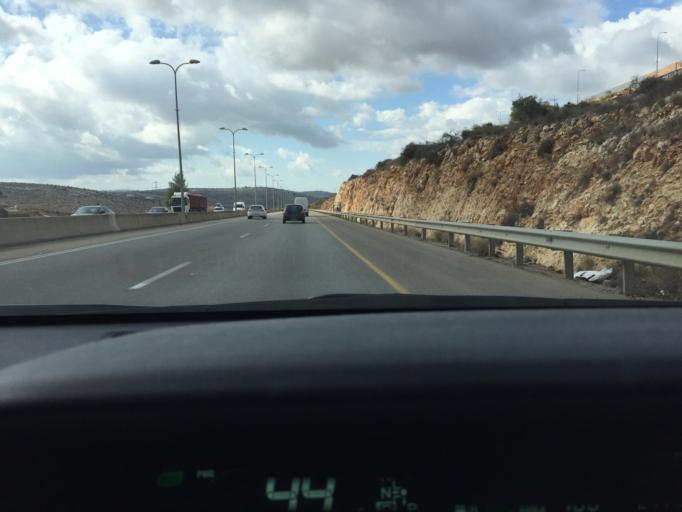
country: IL
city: Revava
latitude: 32.1001
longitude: 35.1208
